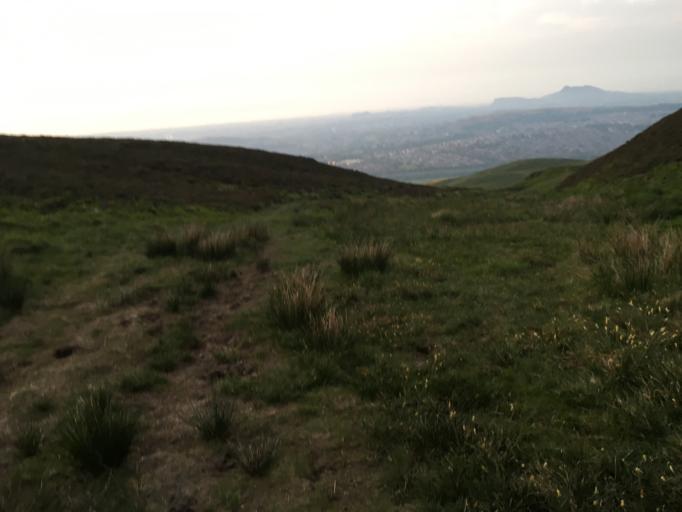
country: GB
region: Scotland
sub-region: Edinburgh
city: Colinton
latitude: 55.8854
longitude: -3.2290
